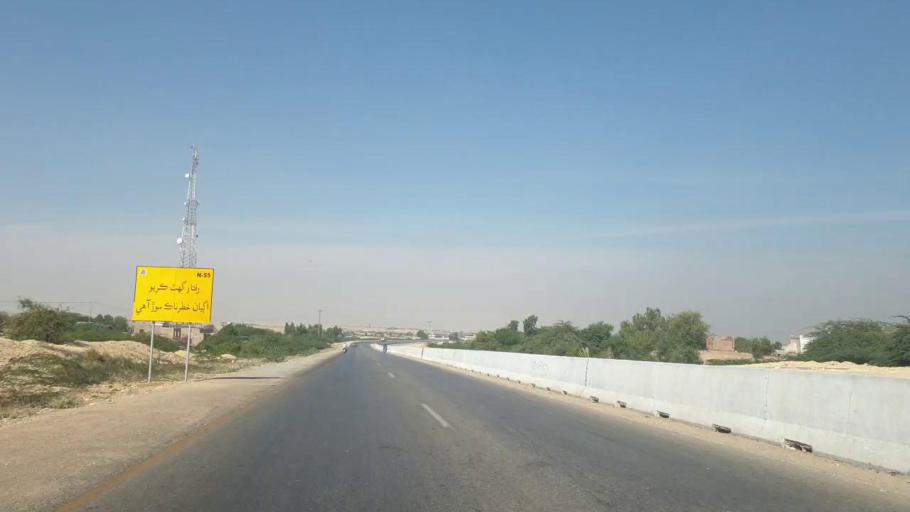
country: PK
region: Sindh
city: Hala
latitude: 25.7170
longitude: 68.2944
